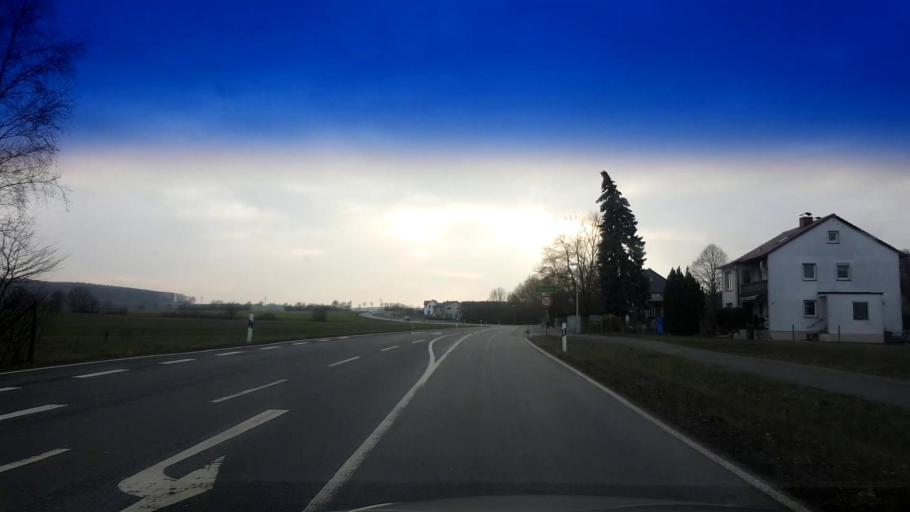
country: DE
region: Bavaria
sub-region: Upper Franconia
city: Hirschaid
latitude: 49.8024
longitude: 10.9751
